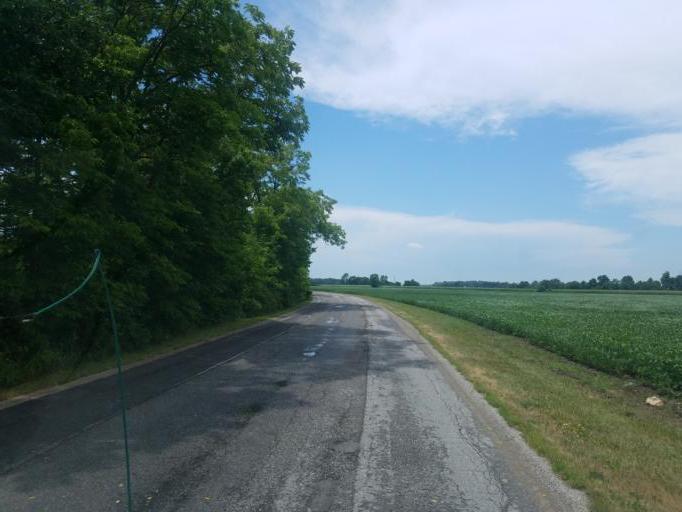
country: US
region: Ohio
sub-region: Paulding County
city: Antwerp
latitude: 41.1987
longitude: -84.7398
